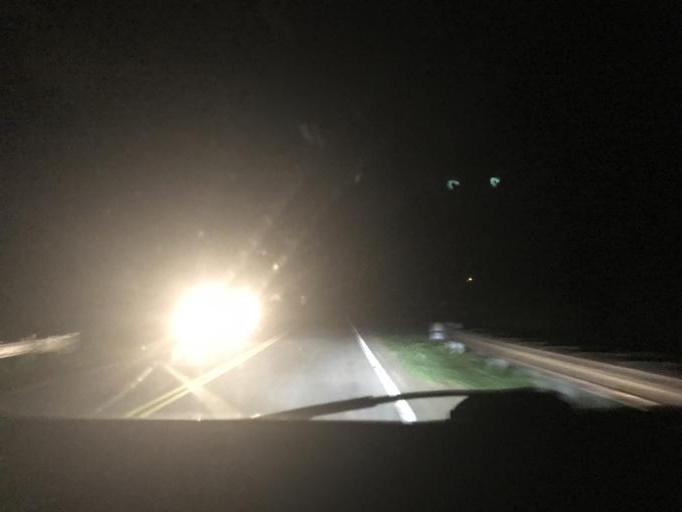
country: US
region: South Carolina
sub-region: Cherokee County
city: East Gaffney
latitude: 35.1535
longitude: -81.6755
